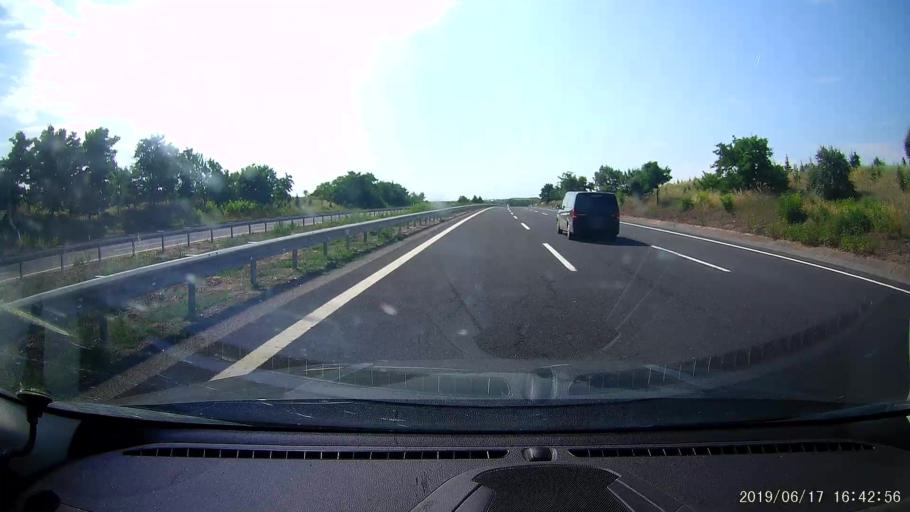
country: TR
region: Kirklareli
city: Luleburgaz
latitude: 41.4768
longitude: 27.3085
